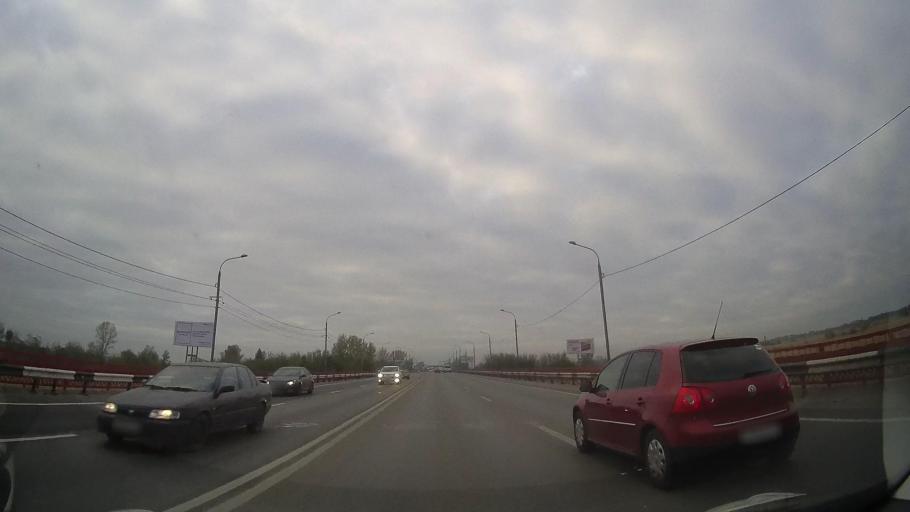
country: RU
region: Rostov
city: Rostov-na-Donu
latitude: 47.2014
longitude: 39.7286
